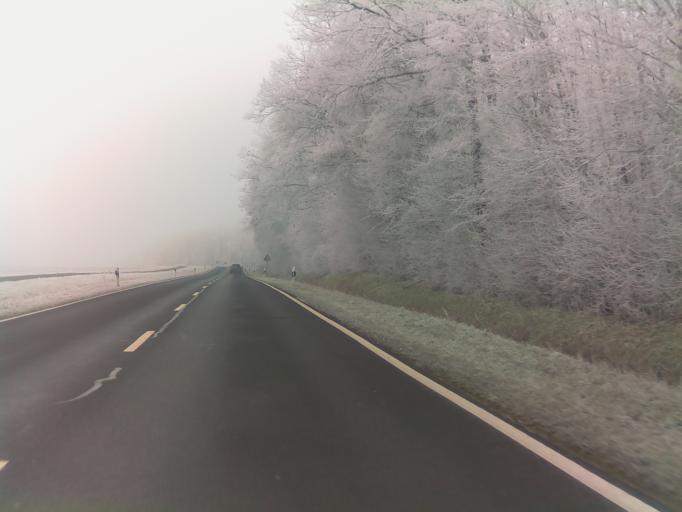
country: DE
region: Bavaria
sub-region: Regierungsbezirk Unterfranken
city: Hassfurt
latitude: 50.0223
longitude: 10.4967
